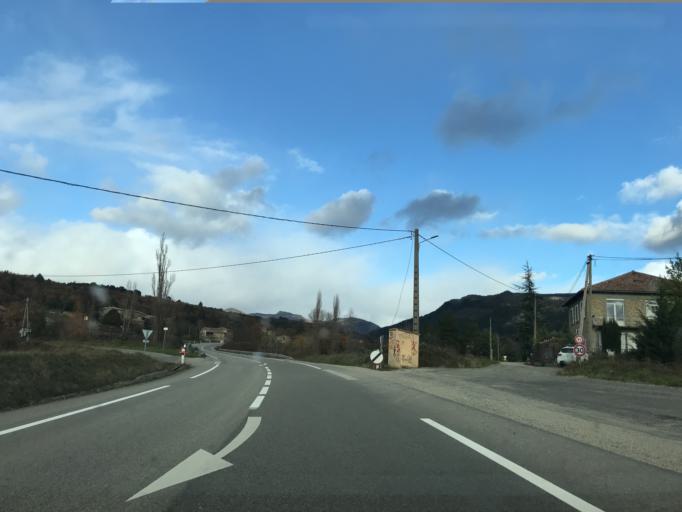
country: FR
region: Rhone-Alpes
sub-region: Departement de l'Ardeche
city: Vesseaux
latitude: 44.6580
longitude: 4.4490
